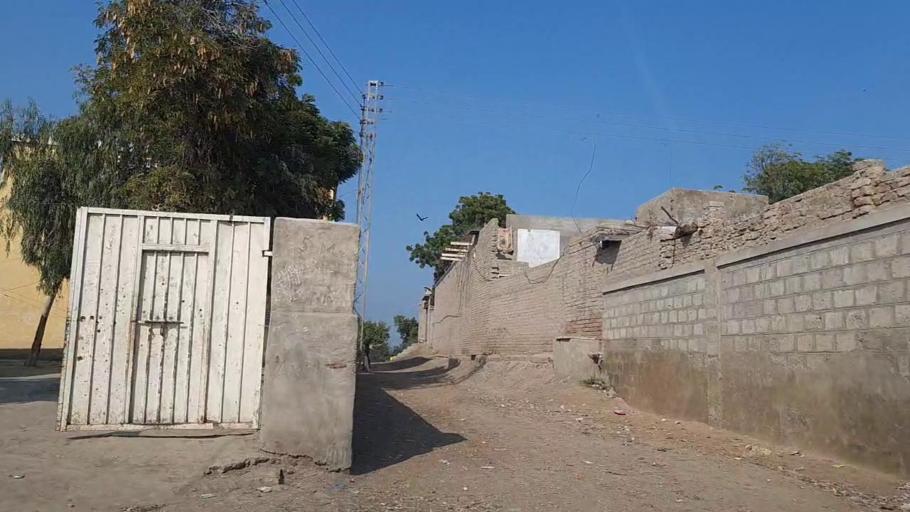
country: PK
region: Sindh
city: Moro
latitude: 26.6852
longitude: 67.9462
